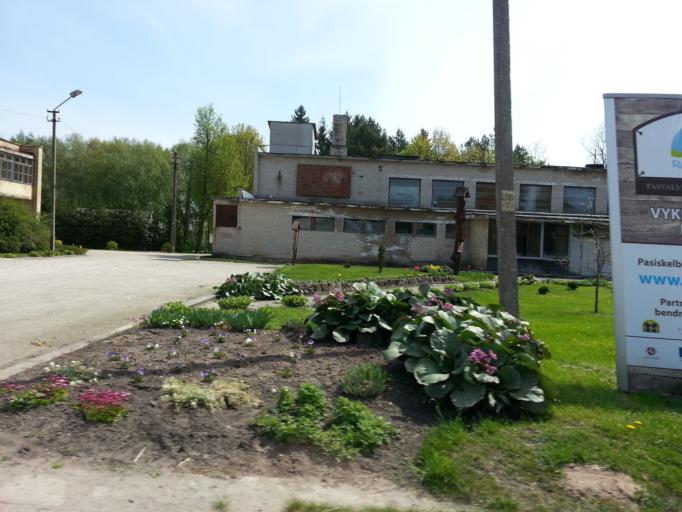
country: LT
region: Panevezys
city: Pasvalys
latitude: 55.9337
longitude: 24.2402
